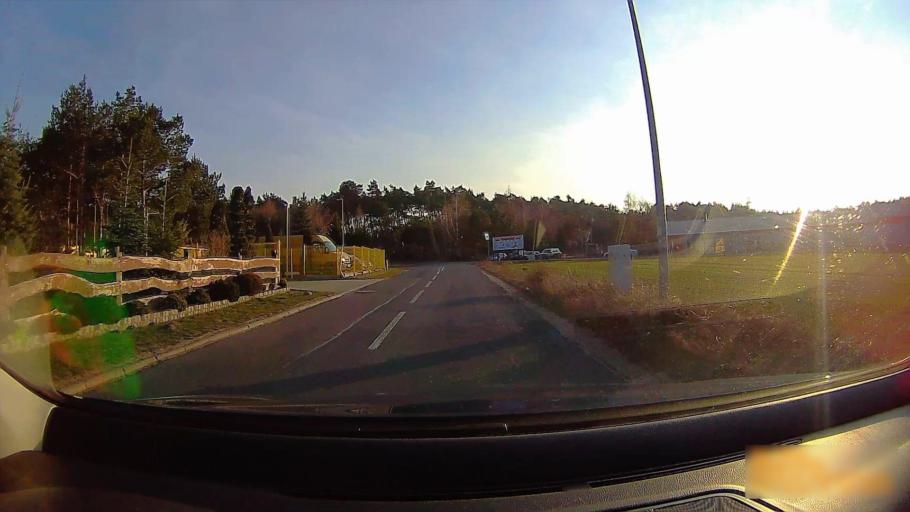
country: PL
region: Greater Poland Voivodeship
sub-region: Konin
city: Konin
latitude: 52.1847
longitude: 18.3317
